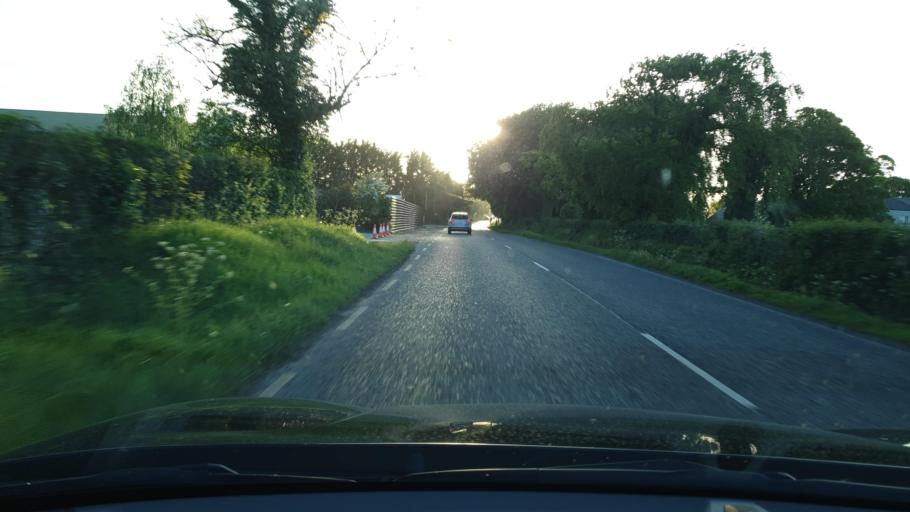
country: IE
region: Leinster
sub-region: An Mhi
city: Ratoath
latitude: 53.5007
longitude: -6.4308
